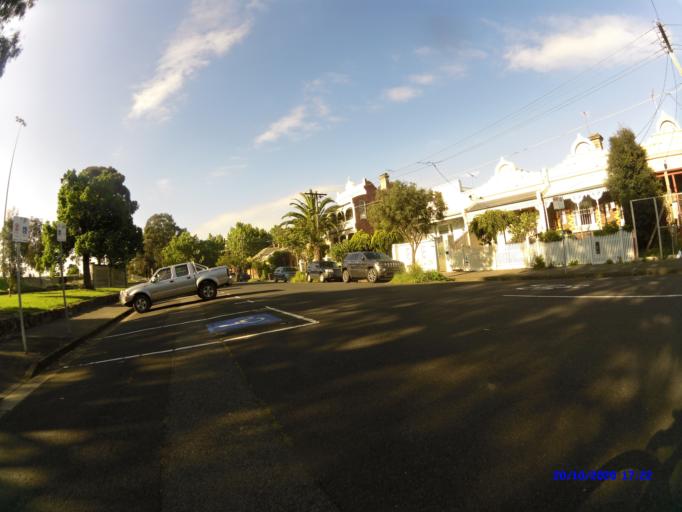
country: AU
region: Victoria
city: Abbotsford
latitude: -37.7990
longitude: 144.9977
